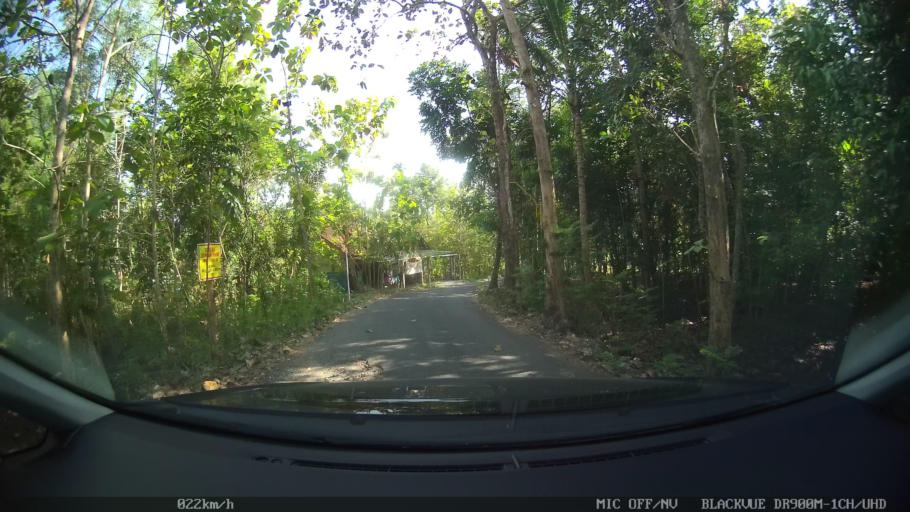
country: ID
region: Daerah Istimewa Yogyakarta
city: Kasihan
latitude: -7.8341
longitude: 110.2856
